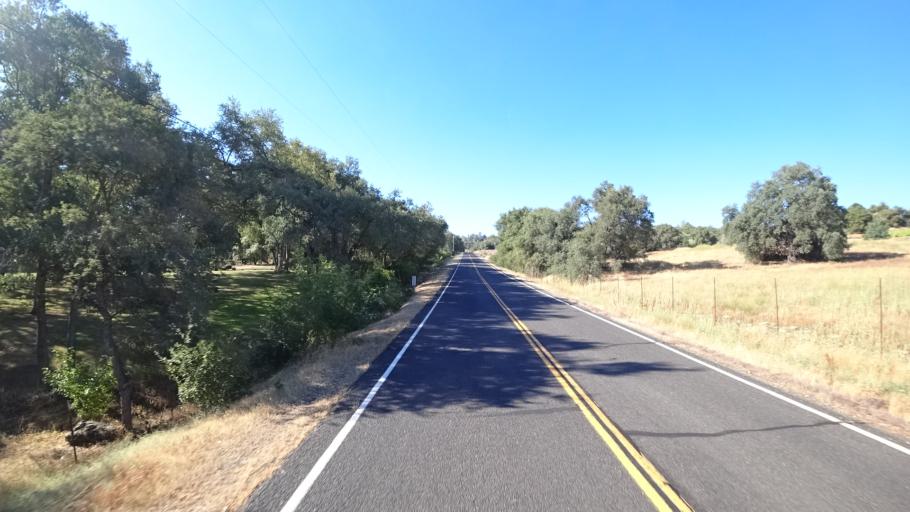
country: US
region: California
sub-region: Calaveras County
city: Murphys
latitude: 38.0915
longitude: -120.4850
